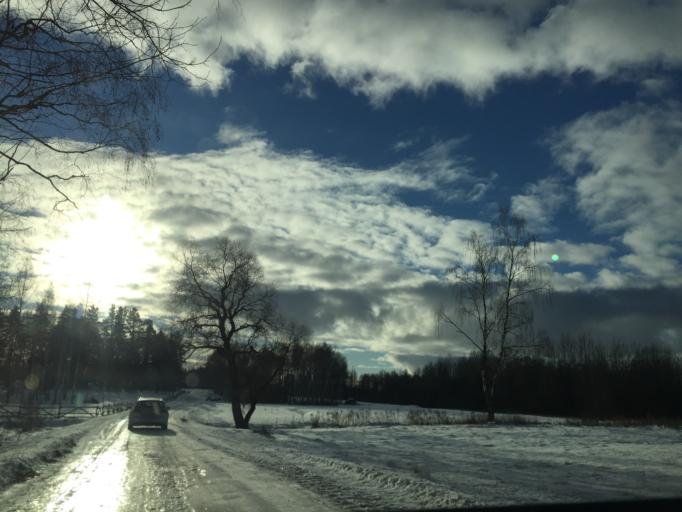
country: LV
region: Lielvarde
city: Lielvarde
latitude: 56.5710
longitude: 24.7983
